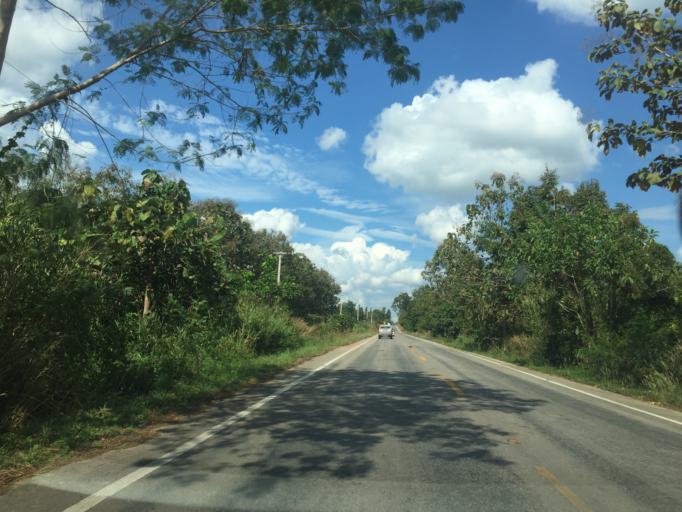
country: TH
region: Lampang
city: Chae Hom
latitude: 18.6929
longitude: 99.4980
